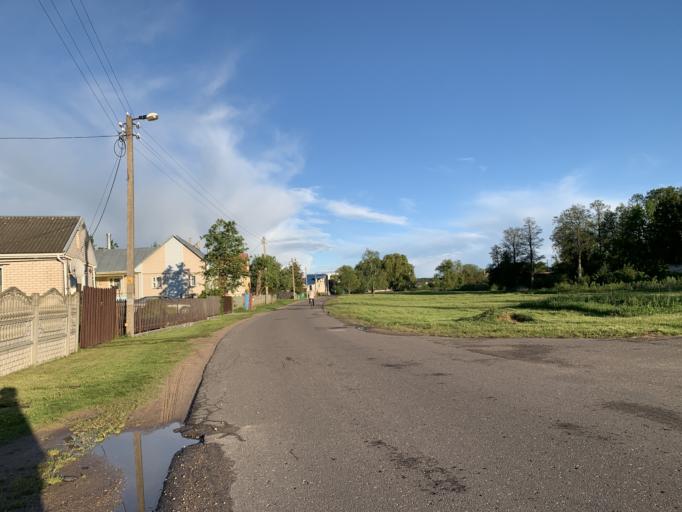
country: BY
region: Minsk
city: Nyasvizh
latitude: 53.2132
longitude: 26.6908
